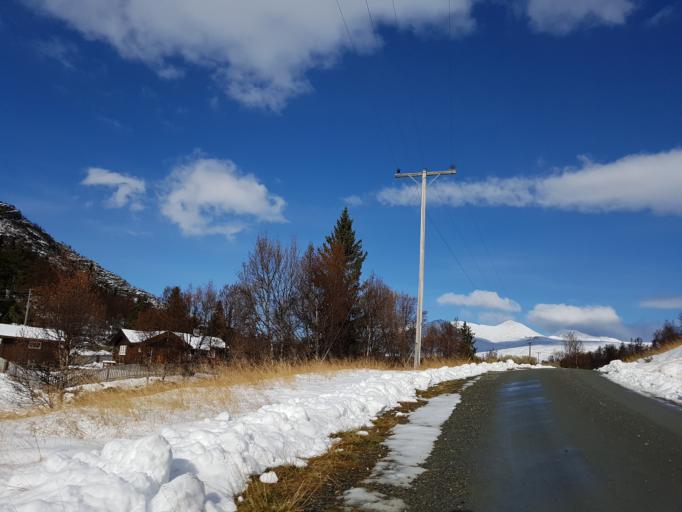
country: NO
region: Oppland
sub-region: Sel
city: Otta
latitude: 61.8189
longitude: 9.6775
